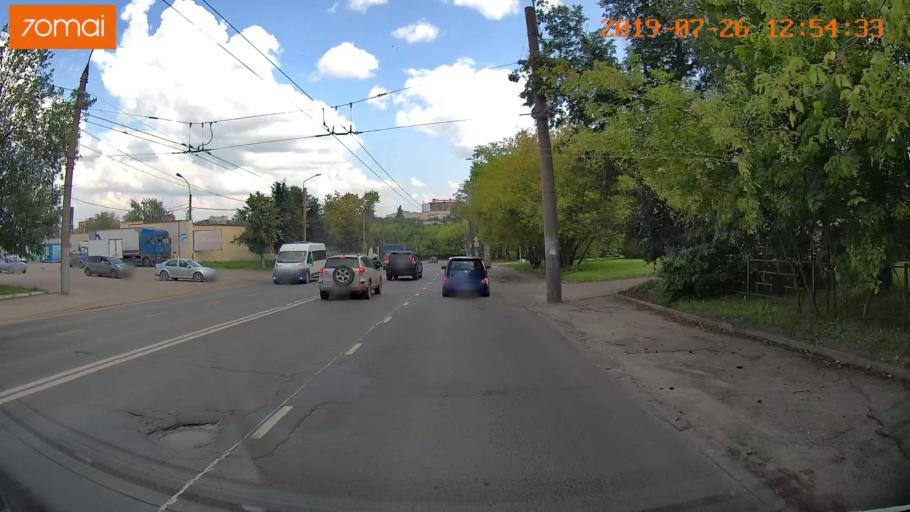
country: RU
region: Ivanovo
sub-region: Gorod Ivanovo
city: Ivanovo
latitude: 57.0112
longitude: 40.9974
